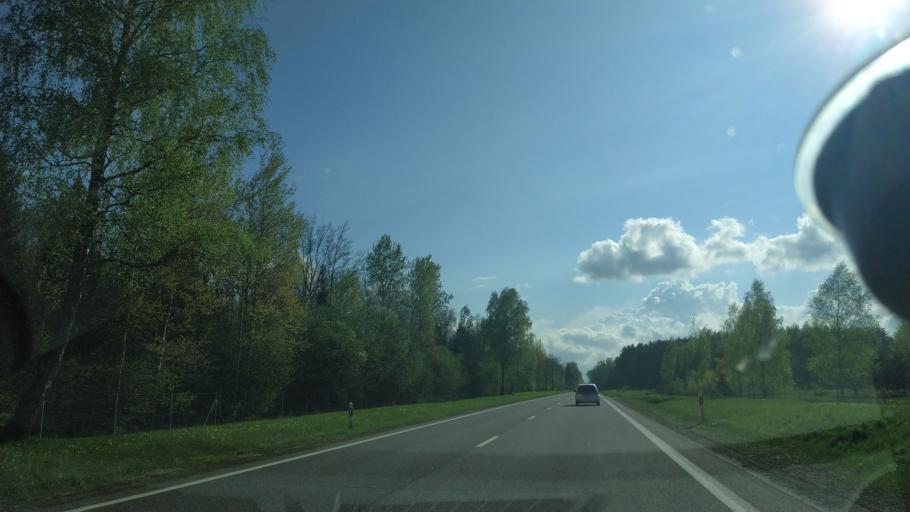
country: LT
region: Kauno apskritis
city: Jonava
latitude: 55.1097
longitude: 24.3508
